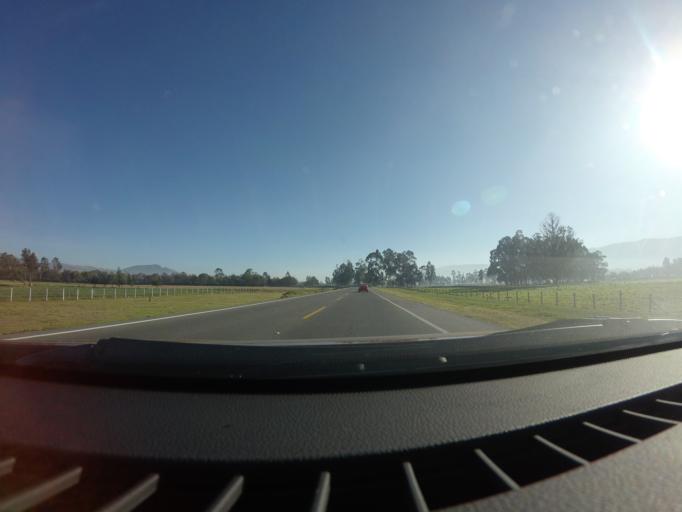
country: CO
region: Cundinamarca
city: Zipaquira
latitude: 5.0152
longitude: -73.9798
